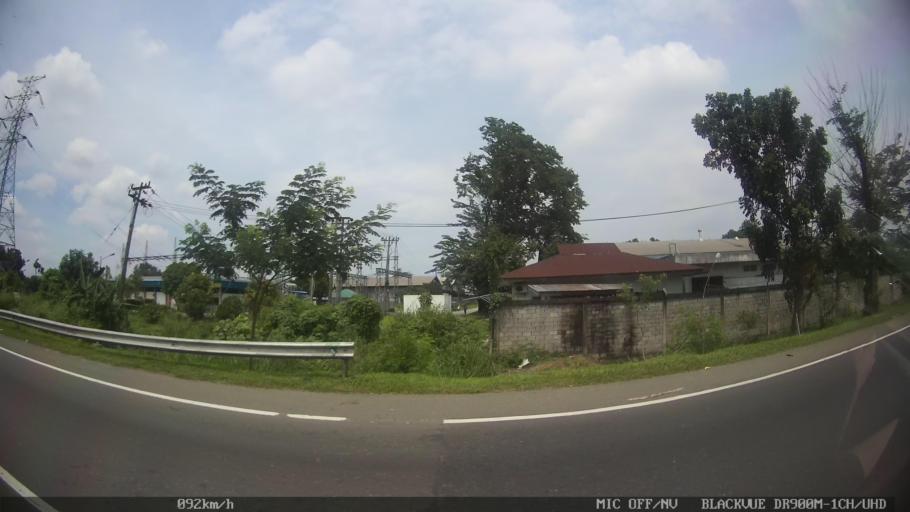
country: ID
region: North Sumatra
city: Labuhan Deli
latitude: 3.6704
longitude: 98.6808
